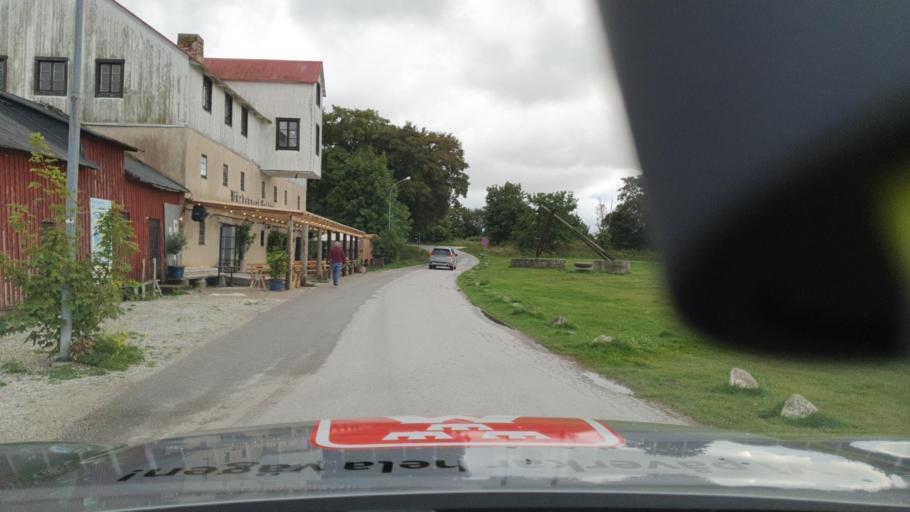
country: SE
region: Gotland
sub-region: Gotland
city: Hemse
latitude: 57.0337
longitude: 18.2581
